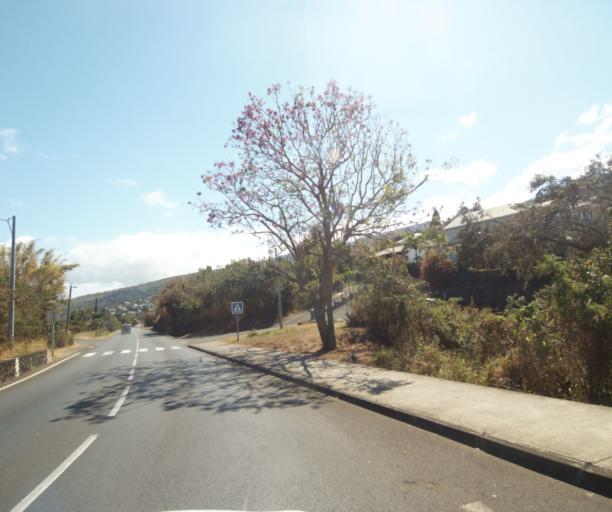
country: RE
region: Reunion
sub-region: Reunion
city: La Possession
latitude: -20.9889
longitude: 55.3309
